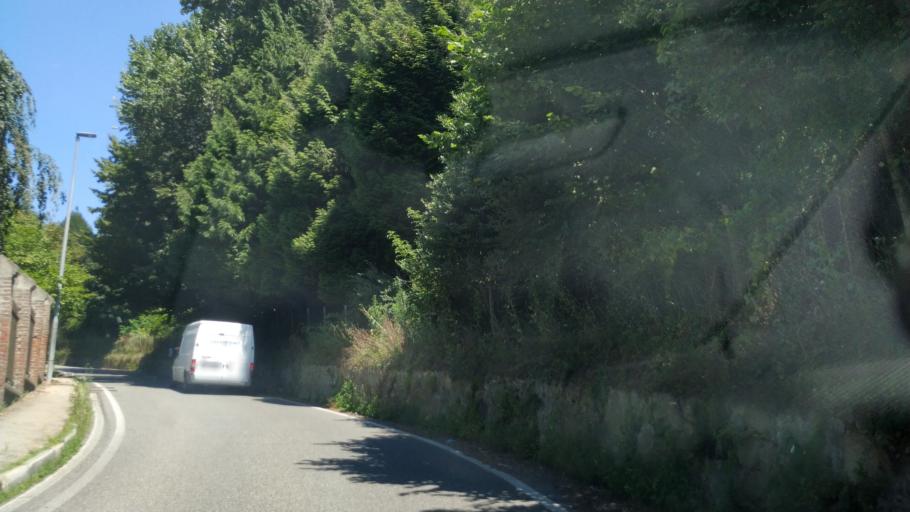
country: IT
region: Piedmont
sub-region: Provincia di Torino
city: San Mauro Torinese
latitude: 45.0838
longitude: 7.7357
